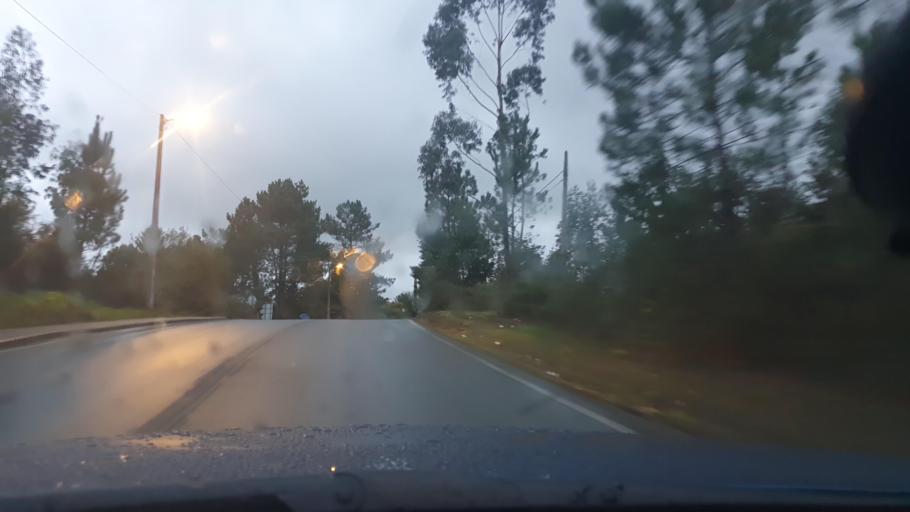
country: ES
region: Galicia
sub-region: Provincia da Coruna
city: Santiago de Compostela
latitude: 42.8470
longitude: -8.5948
